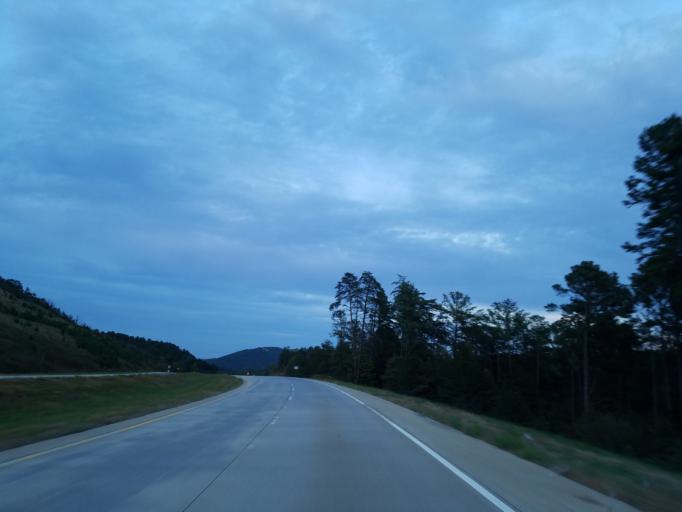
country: US
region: Georgia
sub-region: Bartow County
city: Emerson
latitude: 34.1352
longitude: -84.7536
